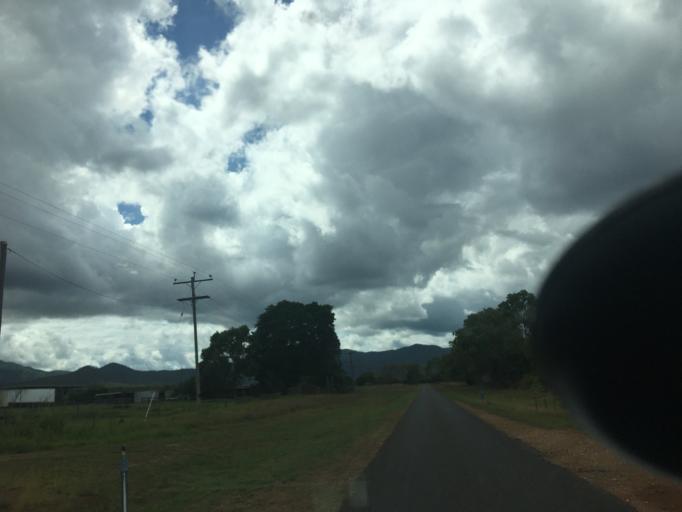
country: AU
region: Queensland
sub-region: Tablelands
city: Mareeba
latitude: -16.9971
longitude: 145.5237
